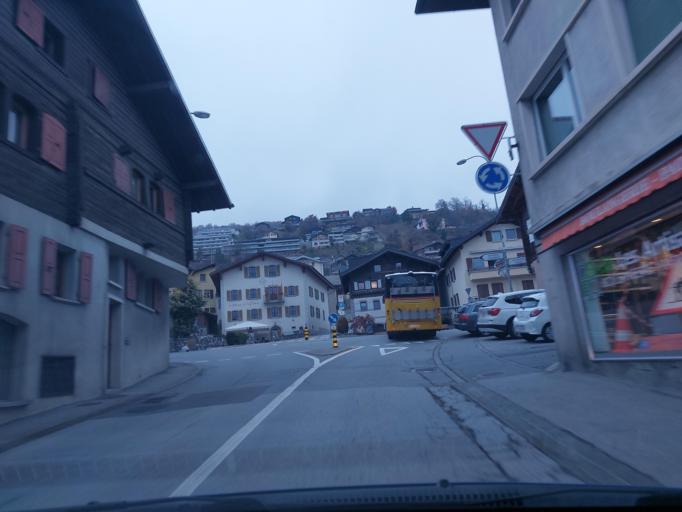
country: CH
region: Valais
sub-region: Sion District
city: Saviese
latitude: 46.2508
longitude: 7.3491
